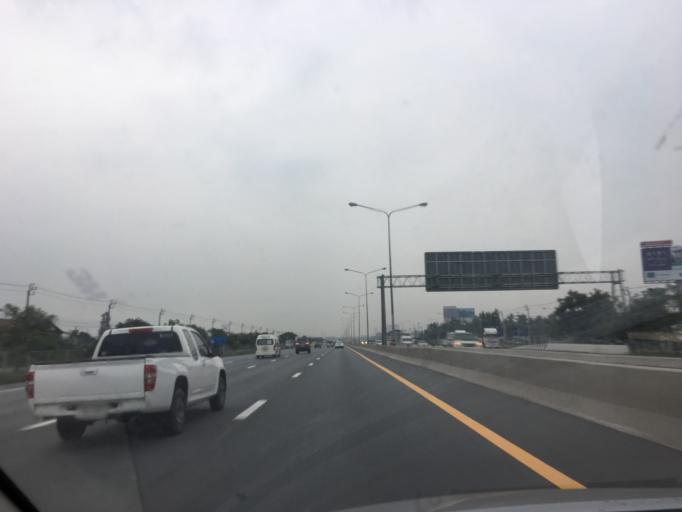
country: TH
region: Bangkok
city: Suan Luang
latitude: 13.6926
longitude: 100.6996
